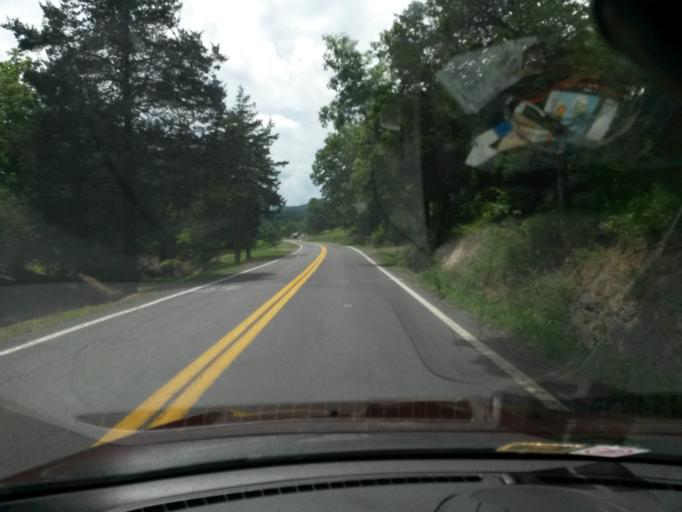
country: US
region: West Virginia
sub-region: Grant County
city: Petersburg
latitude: 38.9652
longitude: -79.1516
